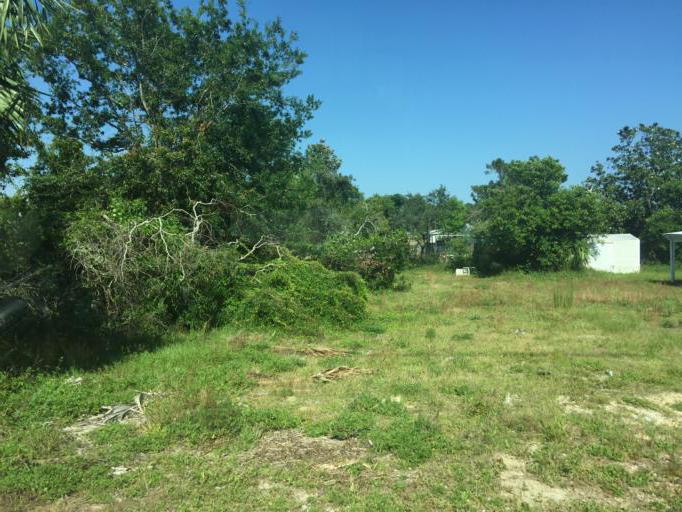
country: US
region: Florida
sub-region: Bay County
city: Panama City Beach
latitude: 30.2030
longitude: -85.8418
